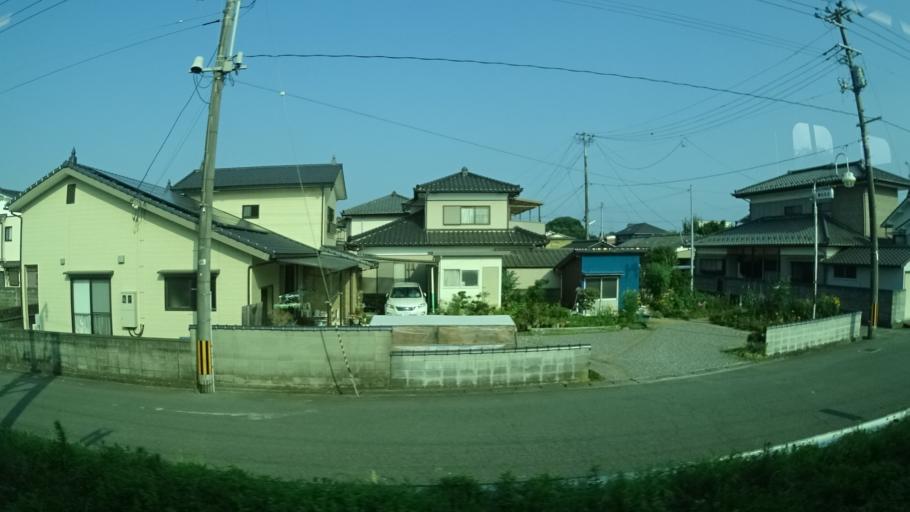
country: JP
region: Ibaraki
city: Kitaibaraki
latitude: 36.9021
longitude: 140.7832
